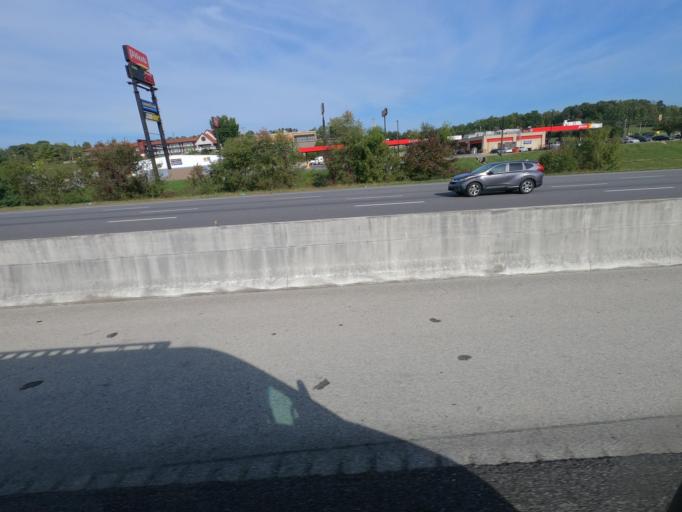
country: US
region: Tennessee
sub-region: Jefferson County
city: Dandridge
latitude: 36.0366
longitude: -83.4435
